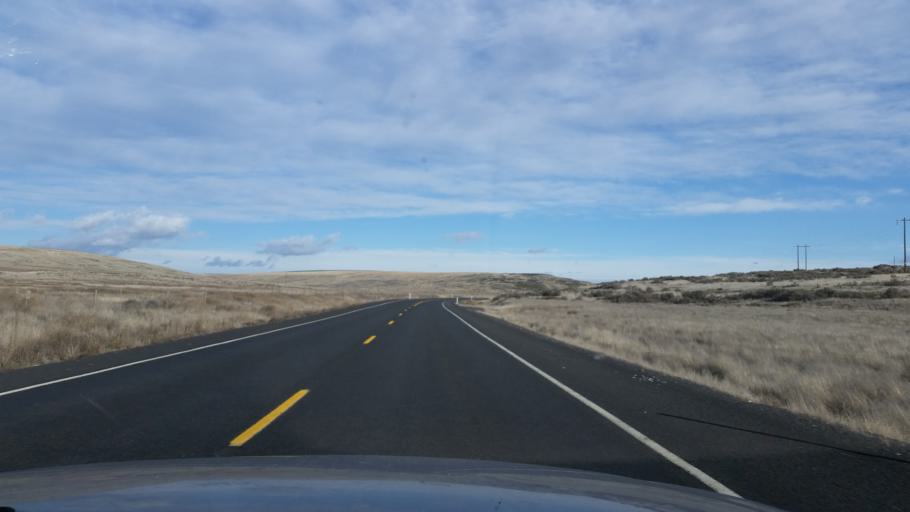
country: US
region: Washington
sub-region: Adams County
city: Ritzville
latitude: 47.3457
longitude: -118.6026
